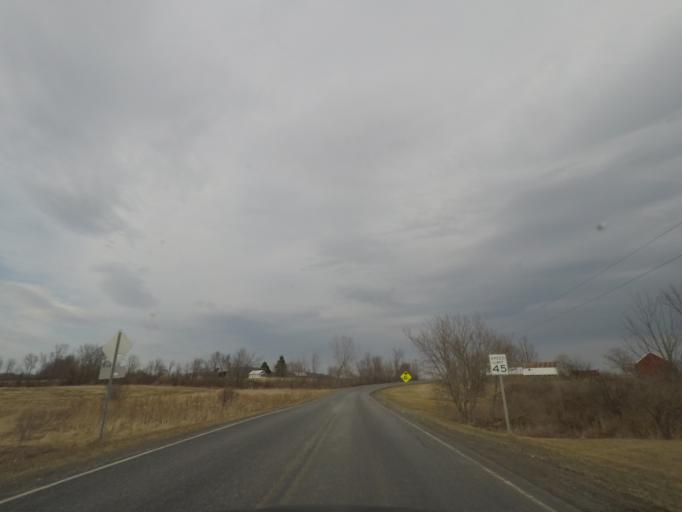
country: US
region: New York
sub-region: Washington County
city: Cambridge
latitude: 42.9670
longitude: -73.4695
